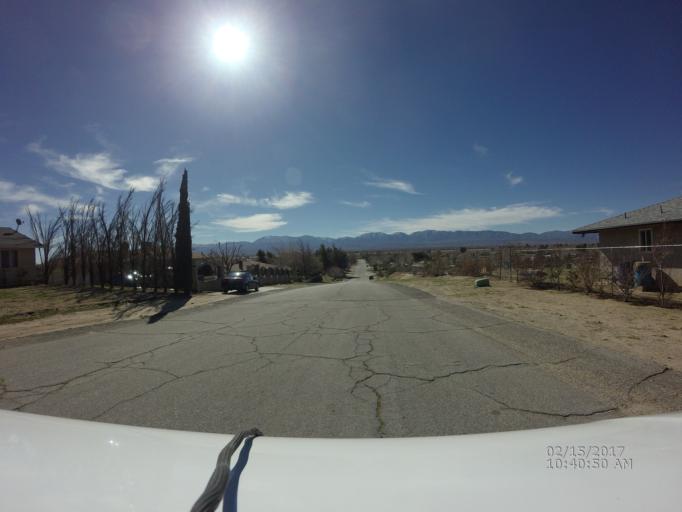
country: US
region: California
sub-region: Los Angeles County
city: Lake Los Angeles
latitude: 34.5856
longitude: -117.8551
